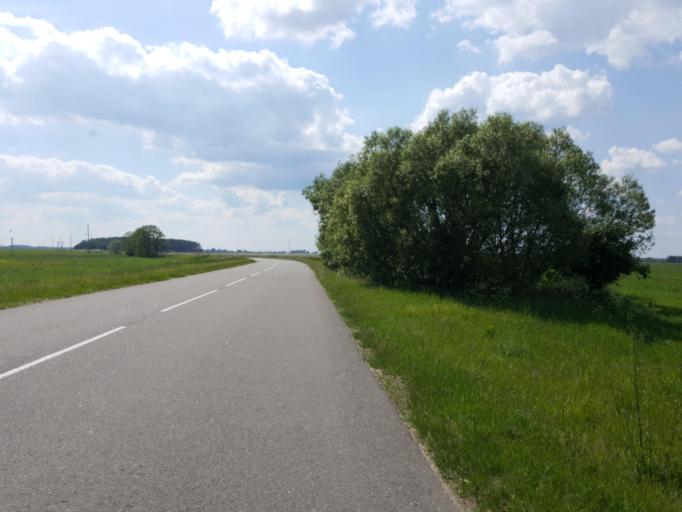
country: BY
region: Brest
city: Kamyanyuki
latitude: 52.5059
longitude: 23.6318
